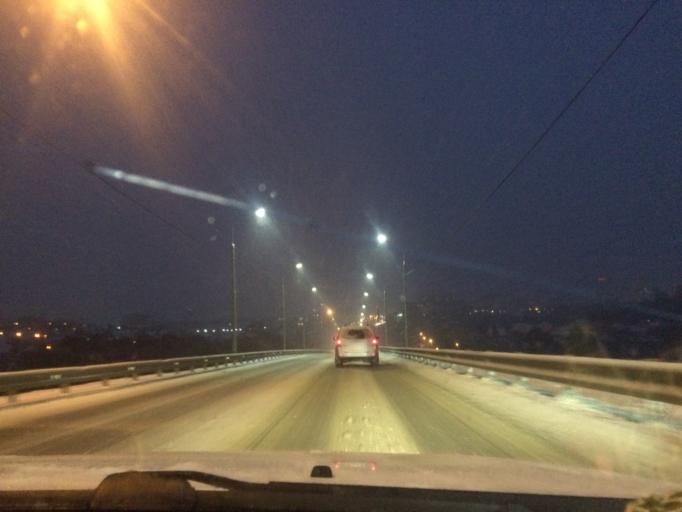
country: RU
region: Tula
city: Mendeleyevskiy
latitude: 54.1576
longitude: 37.5592
